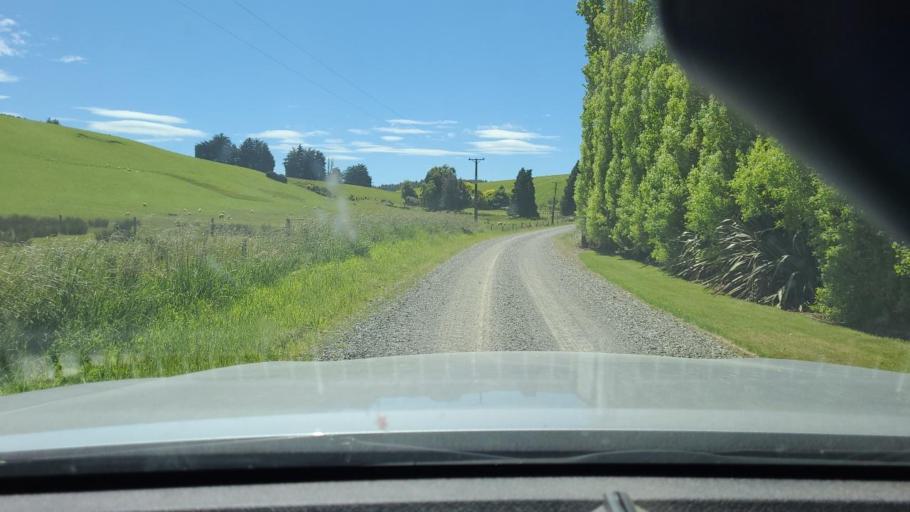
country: NZ
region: Southland
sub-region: Southland District
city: Riverton
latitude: -46.0537
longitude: 167.8561
